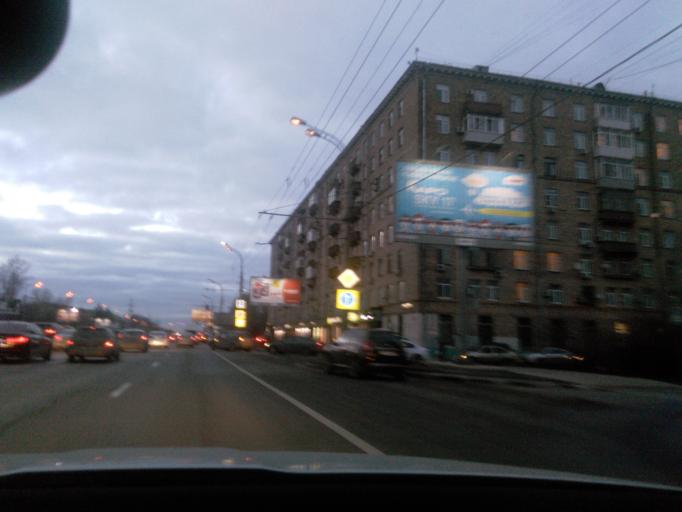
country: RU
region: Moskovskaya
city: Levoberezhnyy
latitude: 55.8327
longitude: 37.4868
